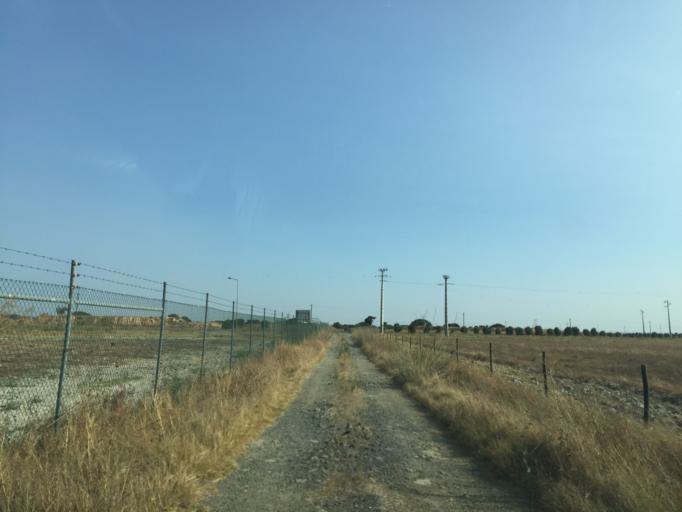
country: PT
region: Beja
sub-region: Aljustrel
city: Aljustrel
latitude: 38.0228
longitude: -8.3582
